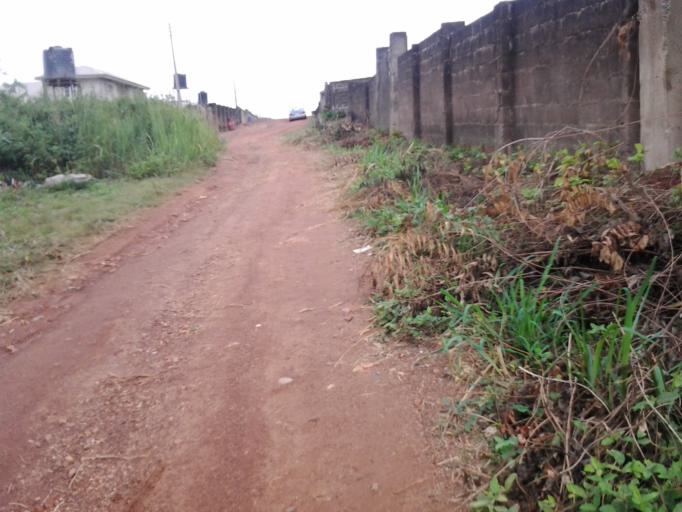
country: NG
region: Oyo
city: Ibadan
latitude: 7.4391
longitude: 3.9567
